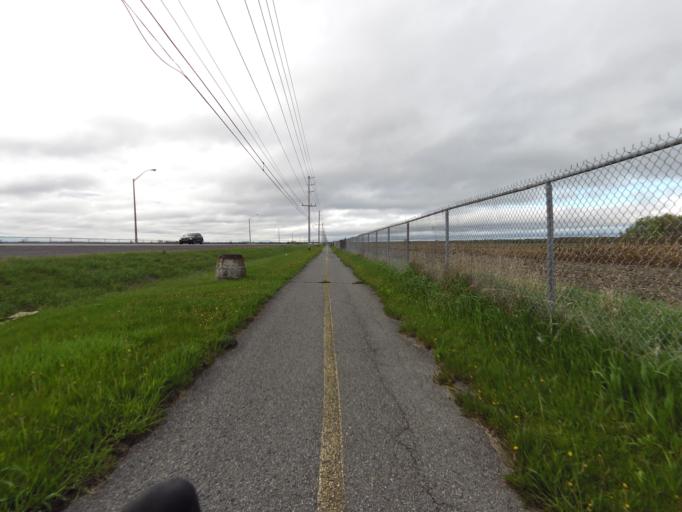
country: CA
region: Ontario
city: Bells Corners
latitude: 45.3134
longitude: -75.7719
